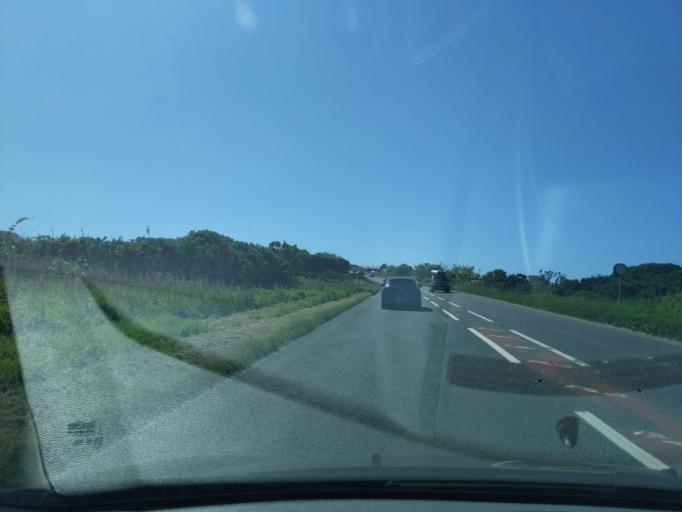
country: GB
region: England
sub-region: Cornwall
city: Perranarworthal
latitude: 50.1654
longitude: -5.1681
